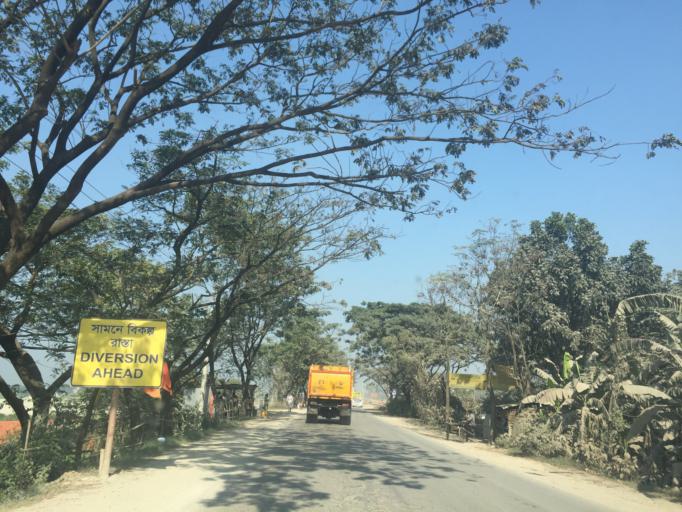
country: BD
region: Dhaka
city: Tungi
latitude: 23.8356
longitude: 90.3401
